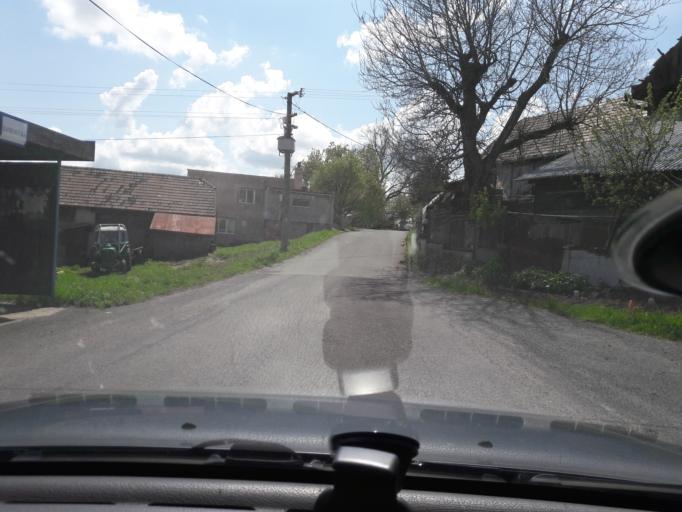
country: SK
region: Banskobystricky
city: Hrinova
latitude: 48.5860
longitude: 19.4734
